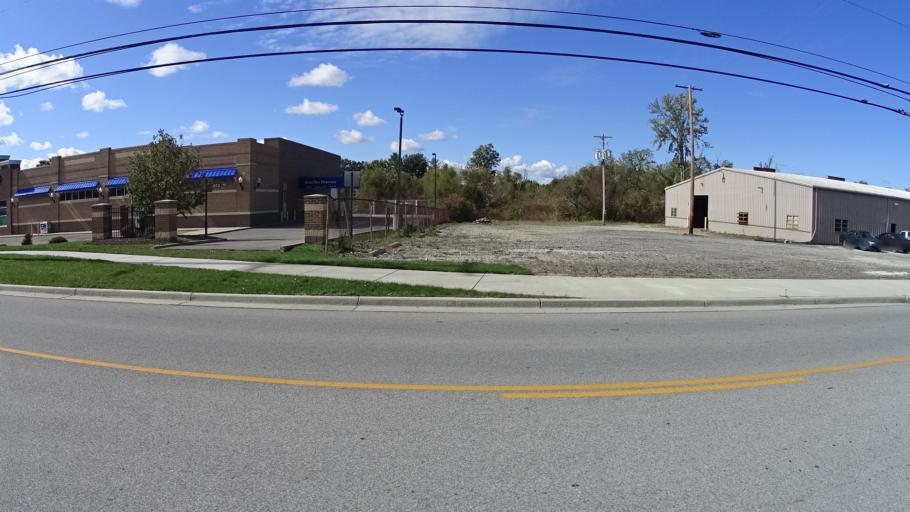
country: US
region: Ohio
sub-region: Lorain County
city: Grafton
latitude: 41.2832
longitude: -82.0638
